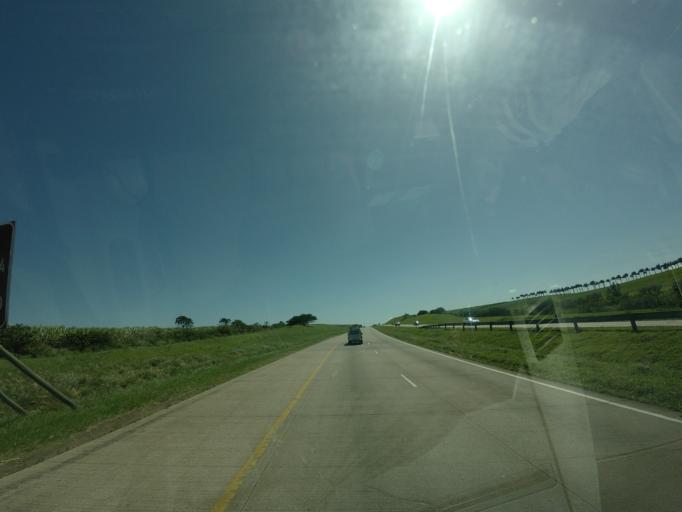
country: ZA
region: KwaZulu-Natal
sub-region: iLembe District Municipality
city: Ballitoville
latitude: -29.4445
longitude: 31.2554
